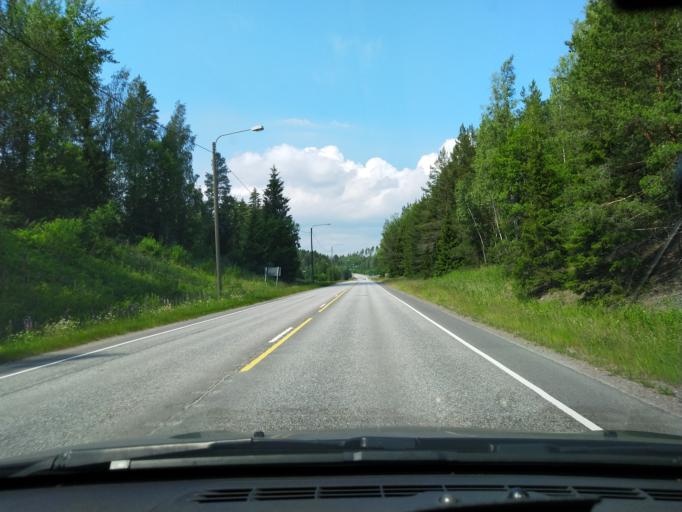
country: FI
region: Uusimaa
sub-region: Helsinki
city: Saukkola
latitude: 60.3810
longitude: 24.0912
